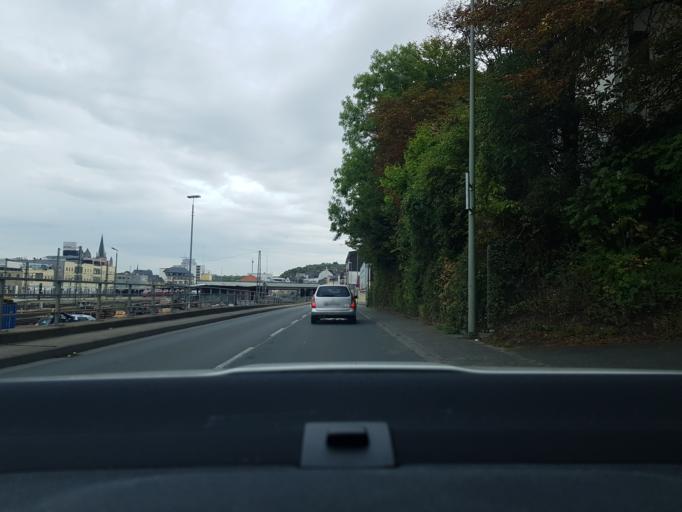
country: DE
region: Hesse
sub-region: Regierungsbezirk Giessen
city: Limburg an der Lahn
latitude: 50.3823
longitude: 8.0592
